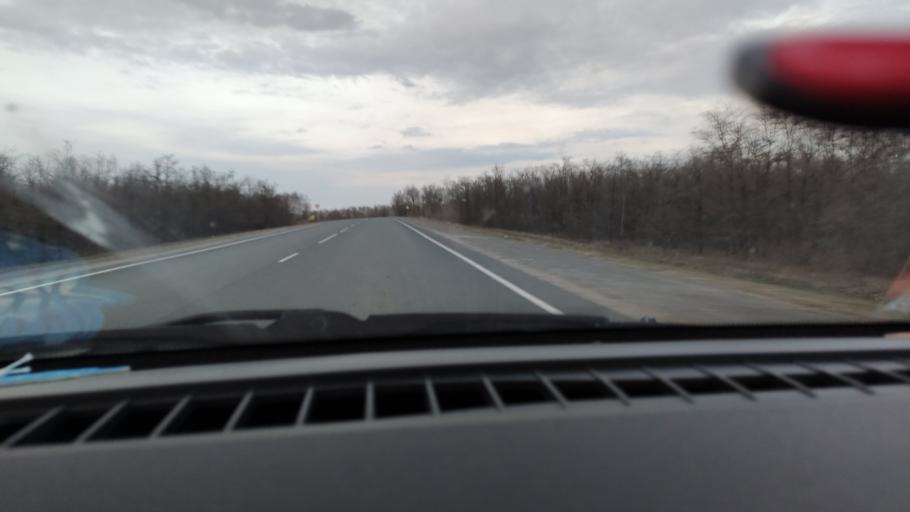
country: RU
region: Saratov
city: Sinodskoye
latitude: 51.9365
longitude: 46.5920
